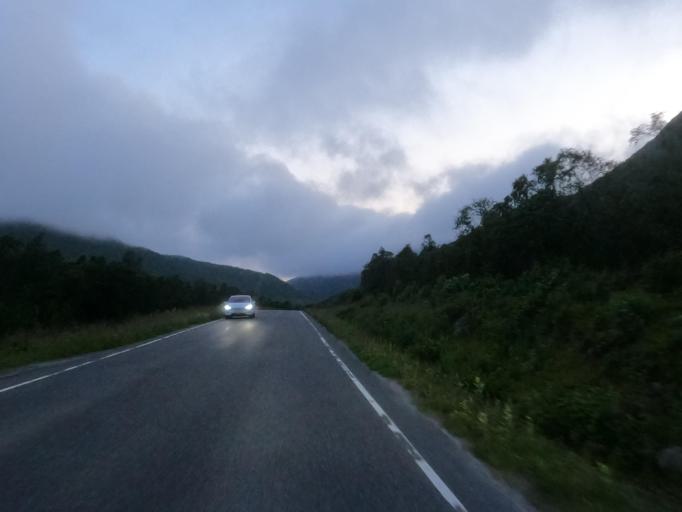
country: NO
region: Nordland
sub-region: Sortland
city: Sortland
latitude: 68.6192
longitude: 15.7180
